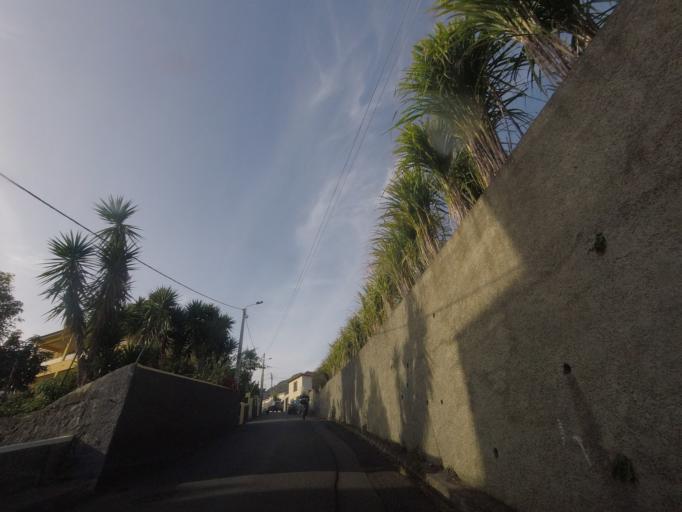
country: PT
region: Madeira
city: Camara de Lobos
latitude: 32.6530
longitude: -16.9862
